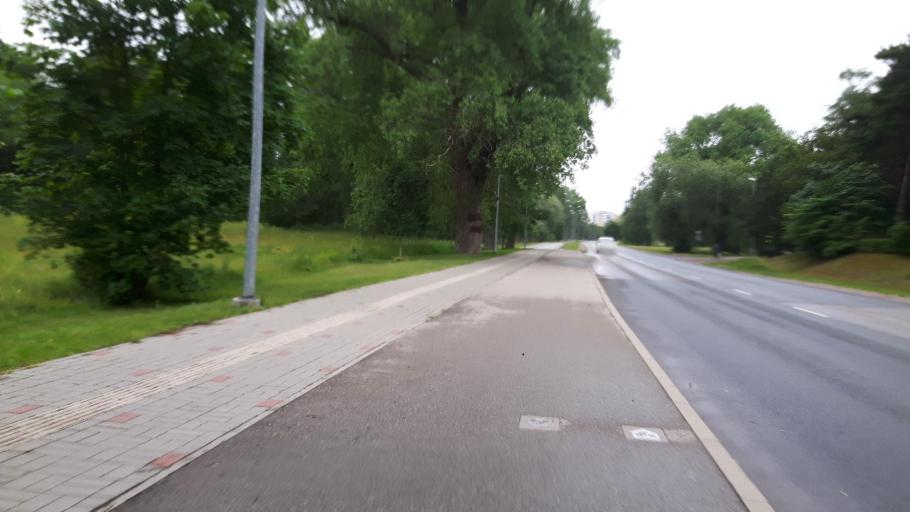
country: LV
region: Liepaja
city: Liepaja
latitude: 56.4809
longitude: 21.0074
